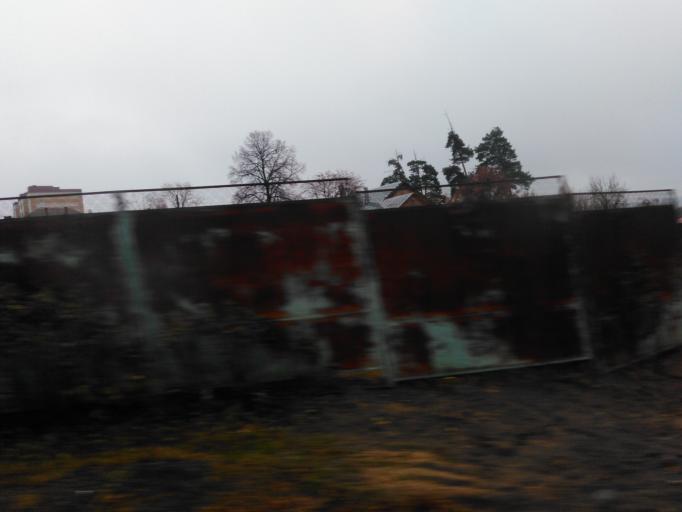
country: RU
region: Tatarstan
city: Osinovo
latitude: 55.8189
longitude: 48.8731
